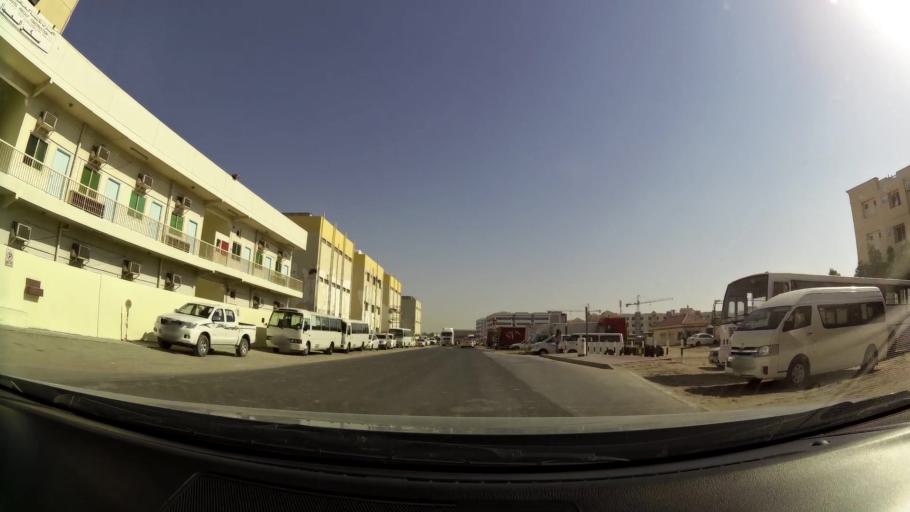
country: AE
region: Dubai
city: Dubai
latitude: 25.0018
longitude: 55.1057
